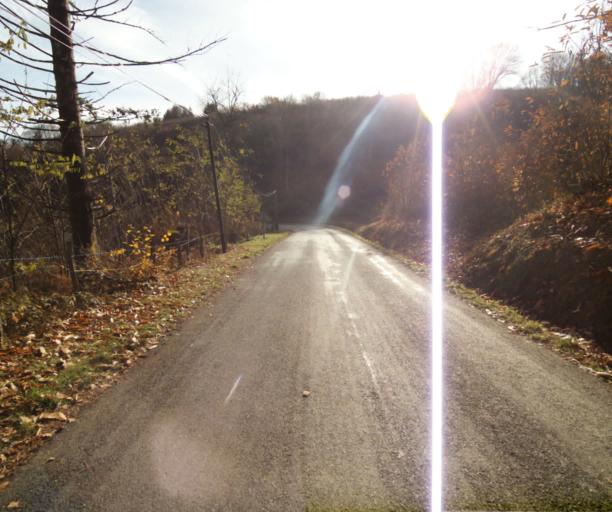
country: FR
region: Limousin
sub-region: Departement de la Correze
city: Sainte-Fortunade
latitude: 45.2091
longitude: 1.7542
